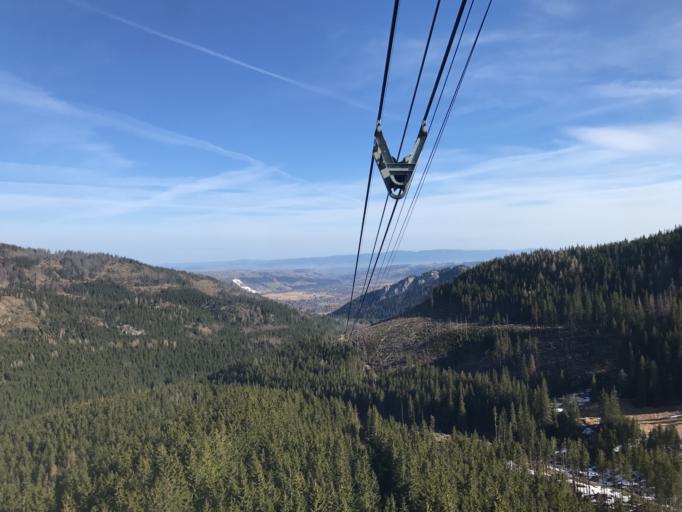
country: PL
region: Lesser Poland Voivodeship
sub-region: Powiat tatrzanski
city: Zakopane
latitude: 49.2536
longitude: 19.9743
